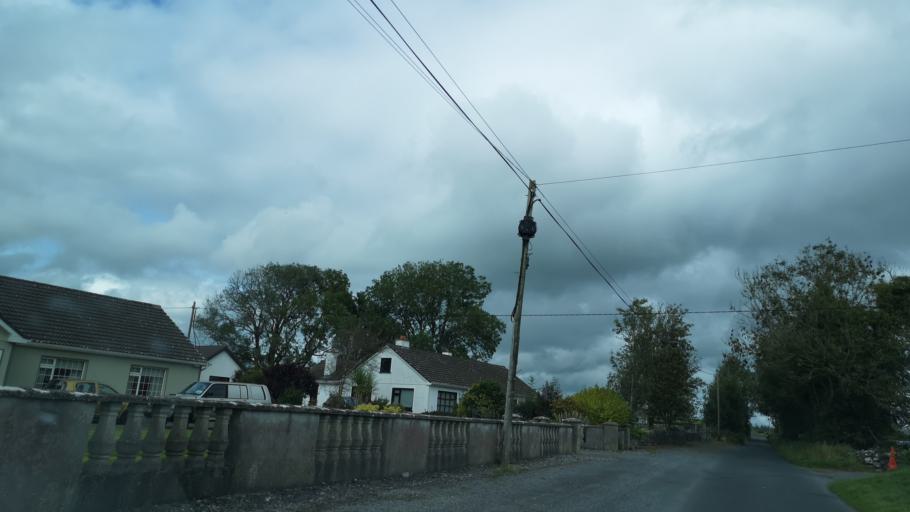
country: IE
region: Connaught
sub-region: County Galway
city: Athenry
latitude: 53.2764
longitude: -8.6719
